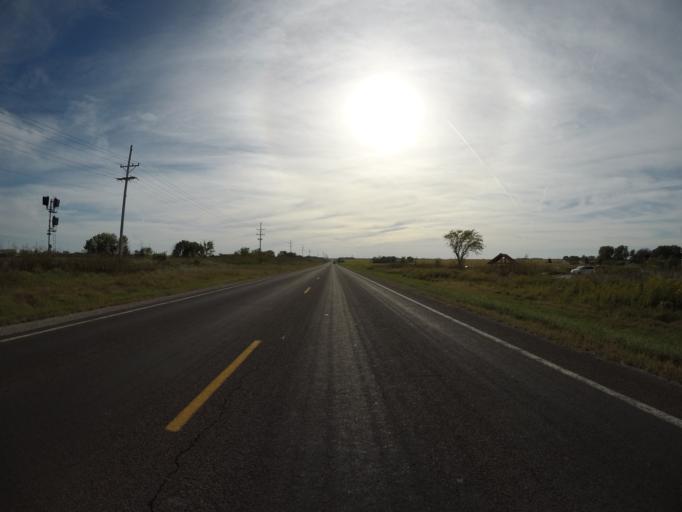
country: US
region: Kansas
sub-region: Johnson County
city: Gardner
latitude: 38.7965
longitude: -94.9611
